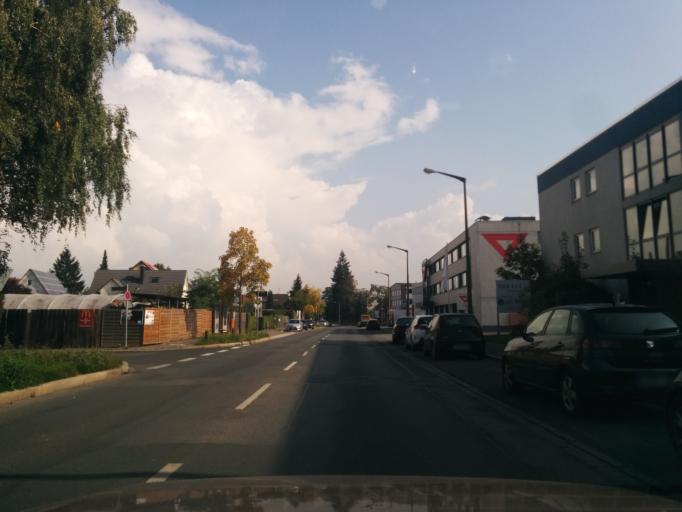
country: DE
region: Bavaria
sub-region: Regierungsbezirk Mittelfranken
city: Nuernberg
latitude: 49.4737
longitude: 11.0853
